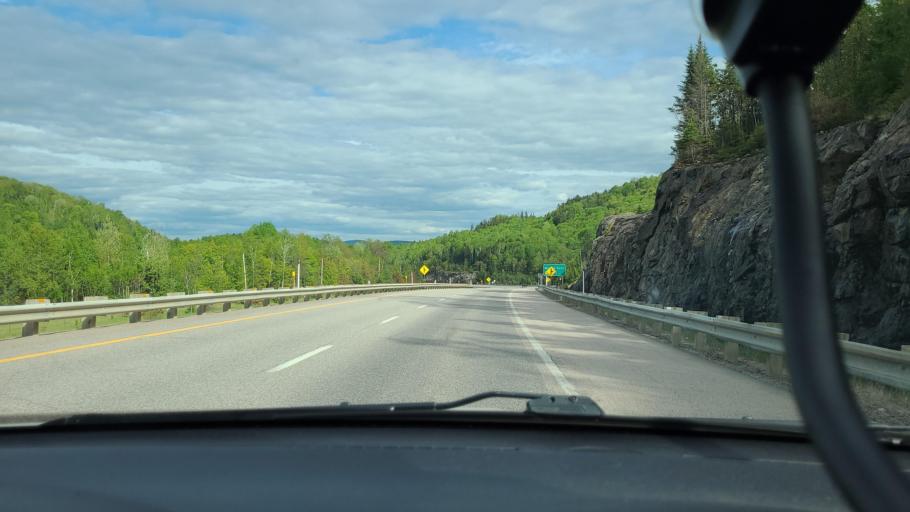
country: CA
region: Quebec
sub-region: Laurentides
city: Mont-Tremblant
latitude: 46.1378
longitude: -74.6331
